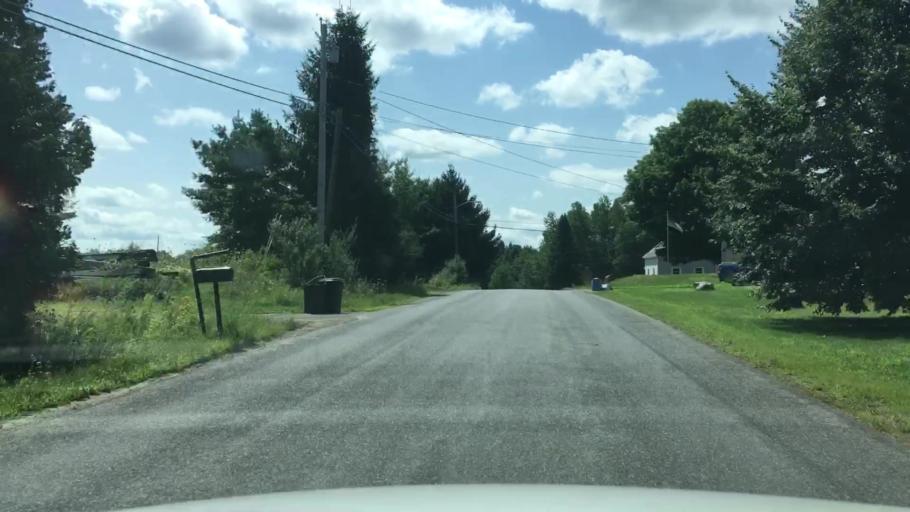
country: US
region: Maine
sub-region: Kennebec County
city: Manchester
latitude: 44.3561
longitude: -69.8166
